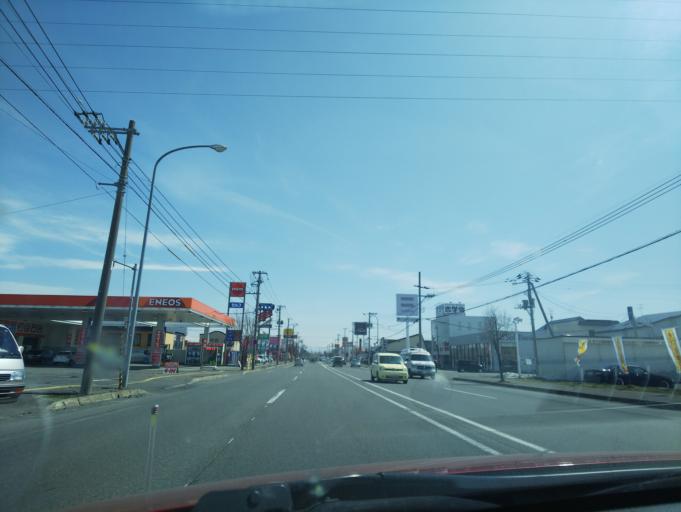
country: JP
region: Hokkaido
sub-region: Asahikawa-shi
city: Asahikawa
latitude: 43.7855
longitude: 142.4109
